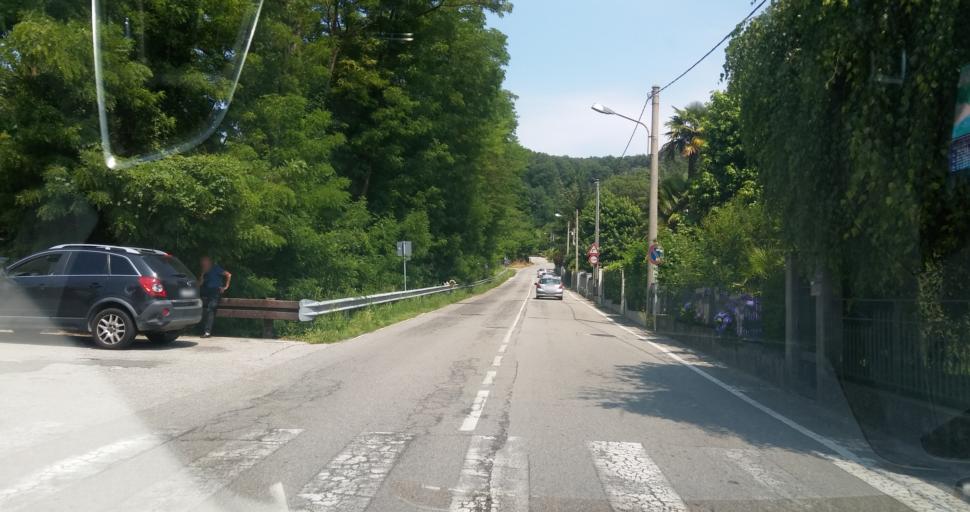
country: IT
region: Lombardy
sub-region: Provincia di Varese
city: Sesto Calende
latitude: 45.7323
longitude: 8.6317
